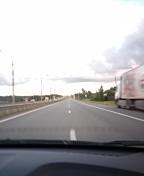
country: RU
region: Moskovskaya
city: Zhukovskiy
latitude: 55.5129
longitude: 38.1322
